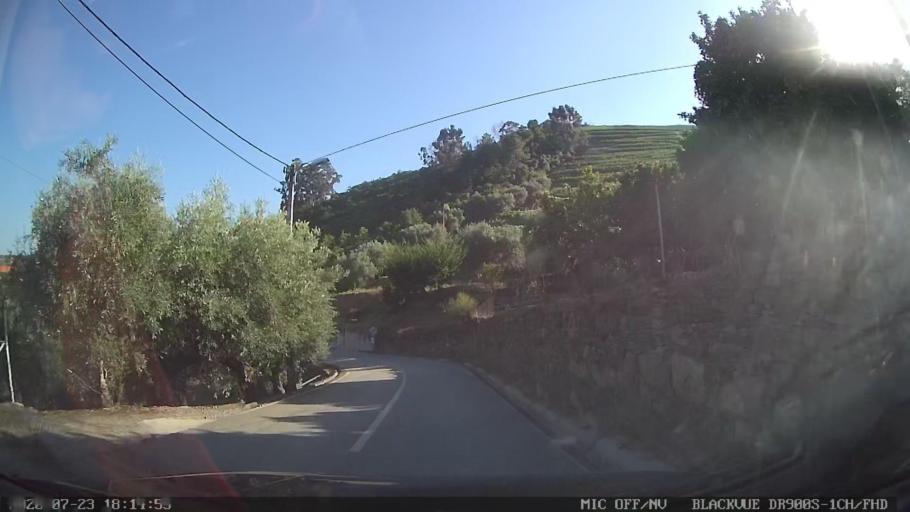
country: PT
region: Viseu
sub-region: Sao Joao da Pesqueira
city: Sao Joao da Pesqueira
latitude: 41.1857
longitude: -7.4194
